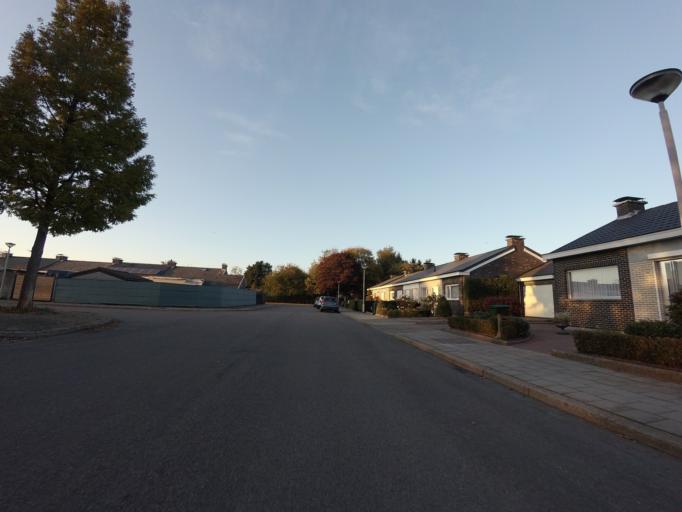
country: BE
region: Flanders
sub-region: Provincie Antwerpen
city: Stabroek
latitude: 51.3535
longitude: 4.3249
